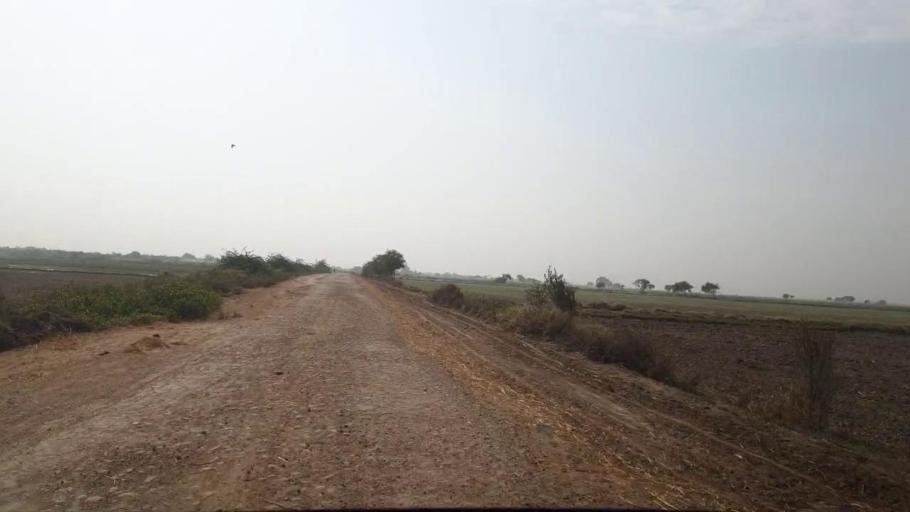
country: PK
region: Sindh
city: Chuhar Jamali
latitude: 24.3838
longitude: 67.9387
